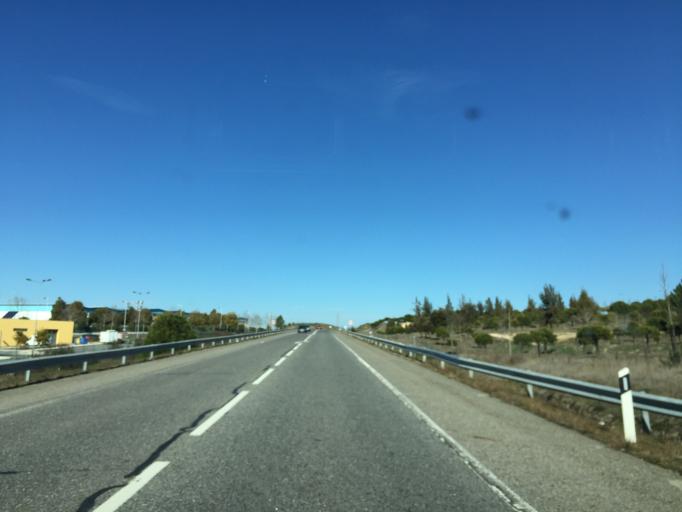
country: PT
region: Castelo Branco
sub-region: Castelo Branco
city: Castelo Branco
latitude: 39.8176
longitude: -7.5180
